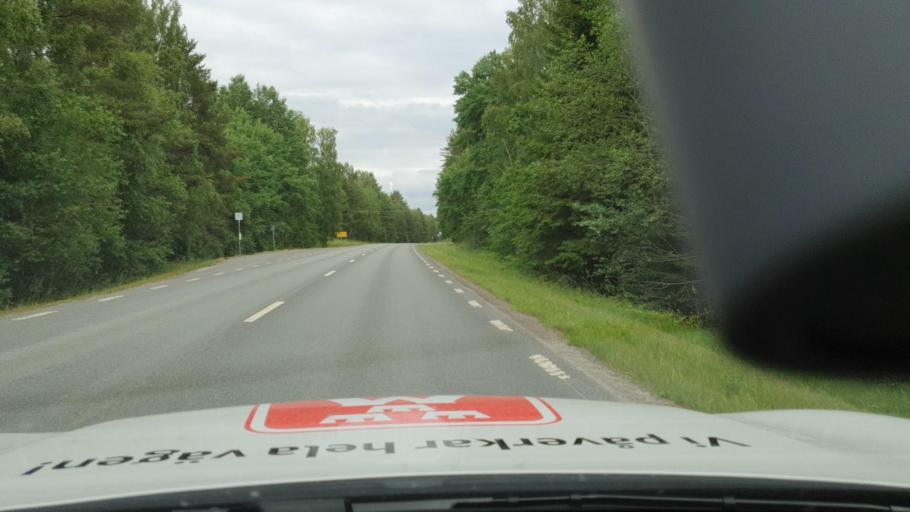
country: SE
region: Vaestra Goetaland
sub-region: Tidaholms Kommun
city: Tidaholm
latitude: 58.1913
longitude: 14.0045
